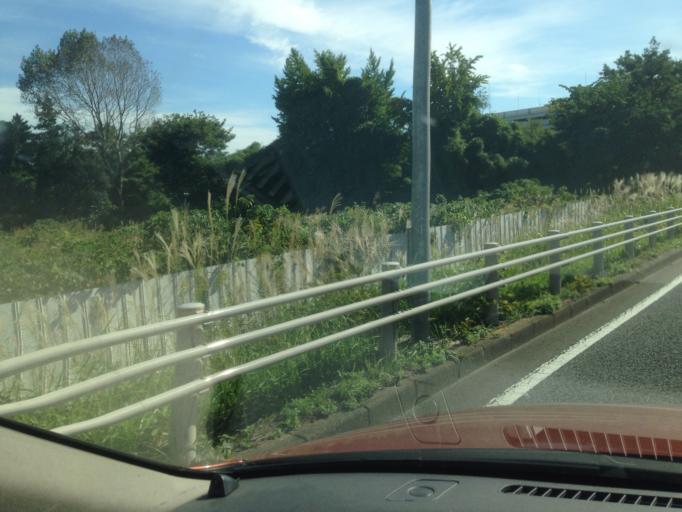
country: JP
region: Tokyo
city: Hachioji
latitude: 35.5836
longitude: 139.3531
